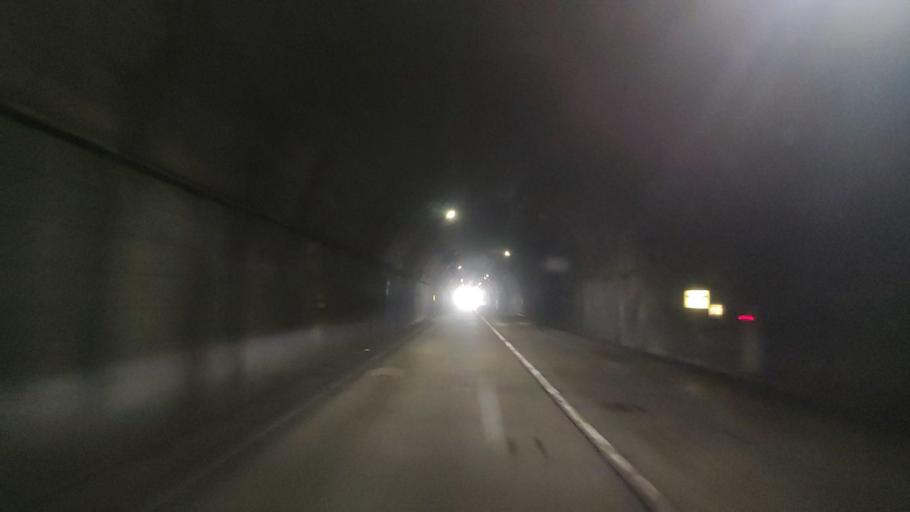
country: JP
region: Mie
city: Owase
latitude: 34.2023
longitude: 136.3297
